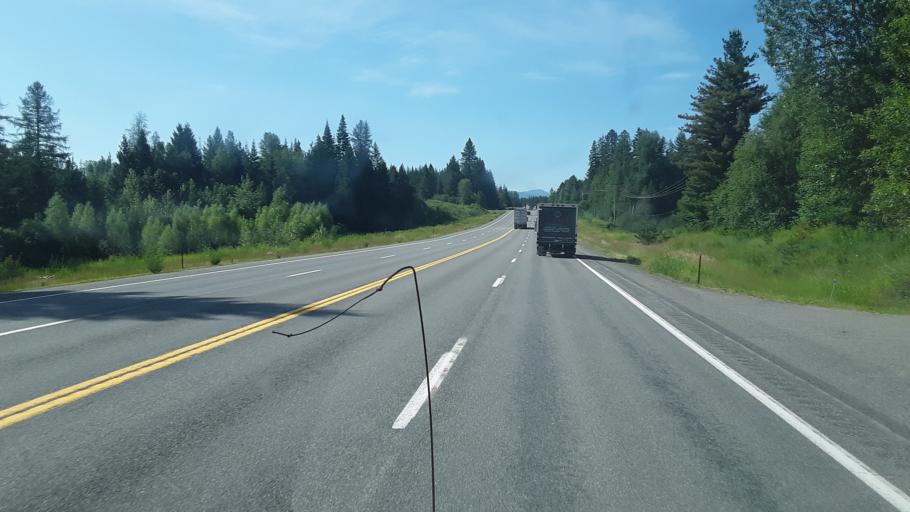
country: US
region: Idaho
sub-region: Bonner County
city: Ponderay
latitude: 48.3430
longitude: -116.5478
